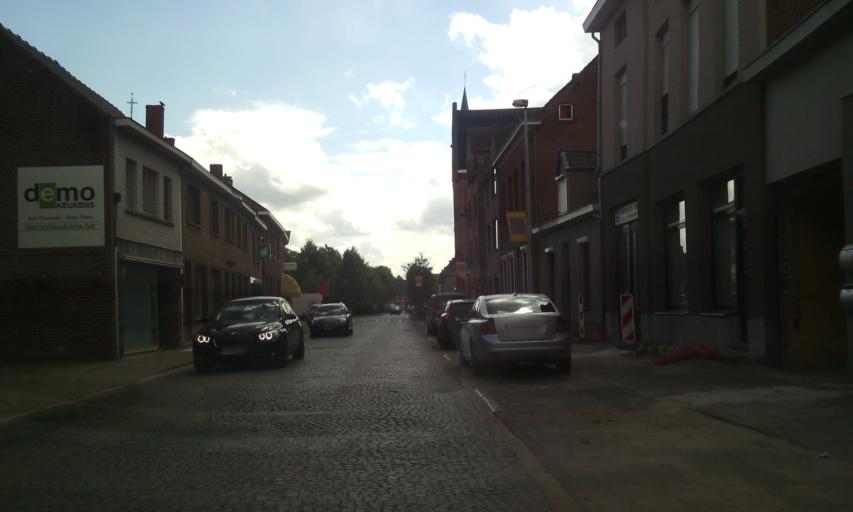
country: BE
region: Flanders
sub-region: Provincie Oost-Vlaanderen
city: Stekene
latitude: 51.1576
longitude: 4.0394
